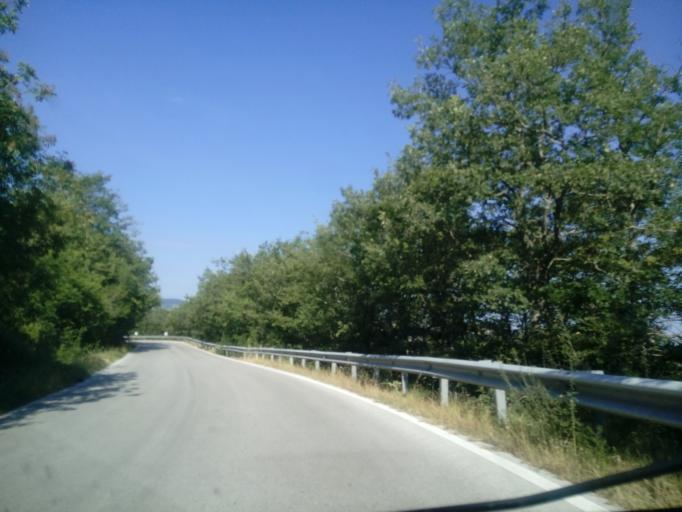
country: IT
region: Molise
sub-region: Provincia di Campobasso
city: Gildone
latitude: 41.5192
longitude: 14.7535
